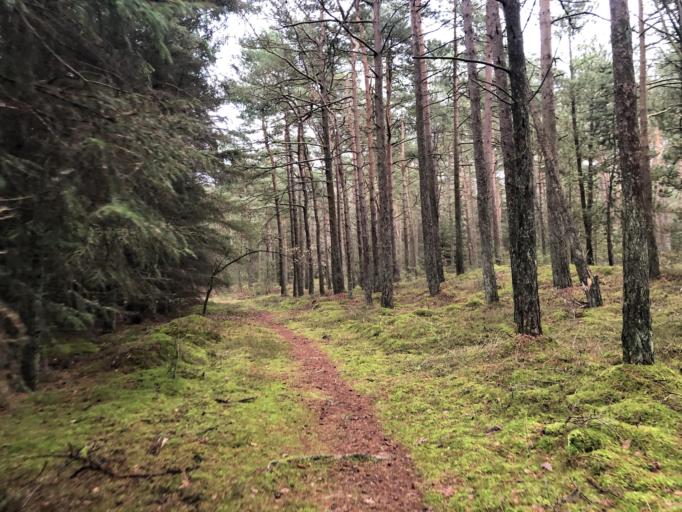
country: DK
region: Central Jutland
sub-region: Holstebro Kommune
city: Ulfborg
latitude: 56.2919
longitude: 8.1680
